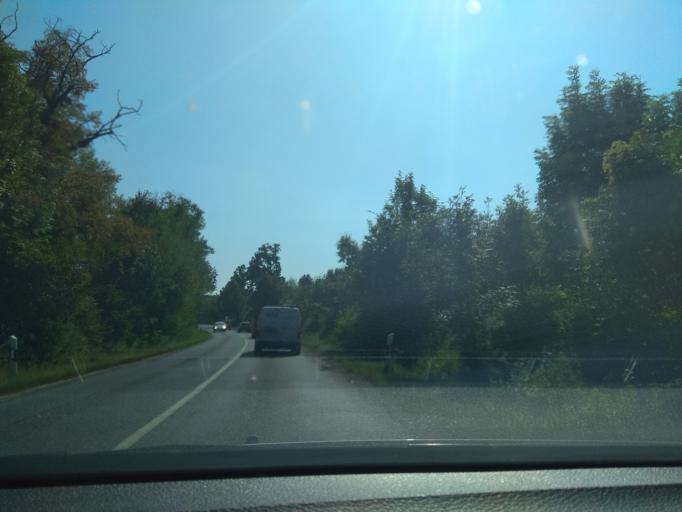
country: HU
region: Borsod-Abauj-Zemplen
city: Harsany
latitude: 48.0015
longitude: 20.7595
